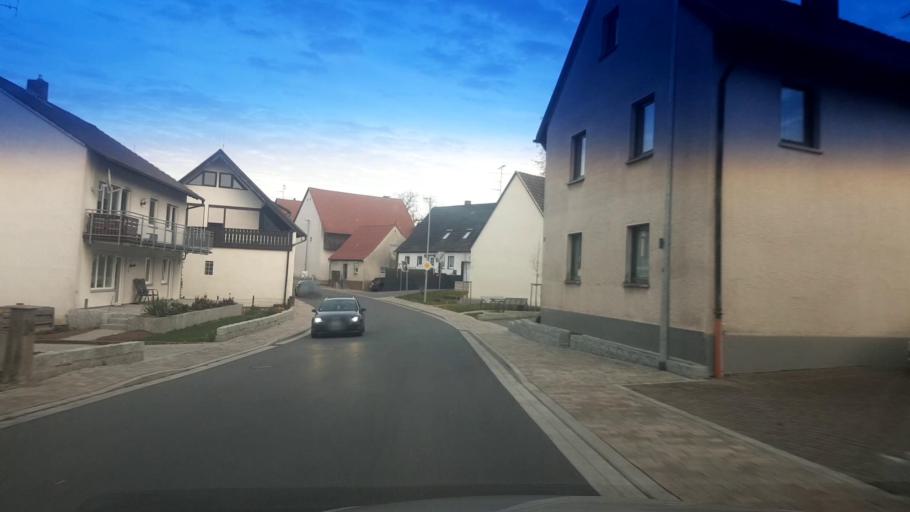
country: DE
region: Bavaria
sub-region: Upper Franconia
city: Viereth-Trunstadt
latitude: 49.9014
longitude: 10.7701
